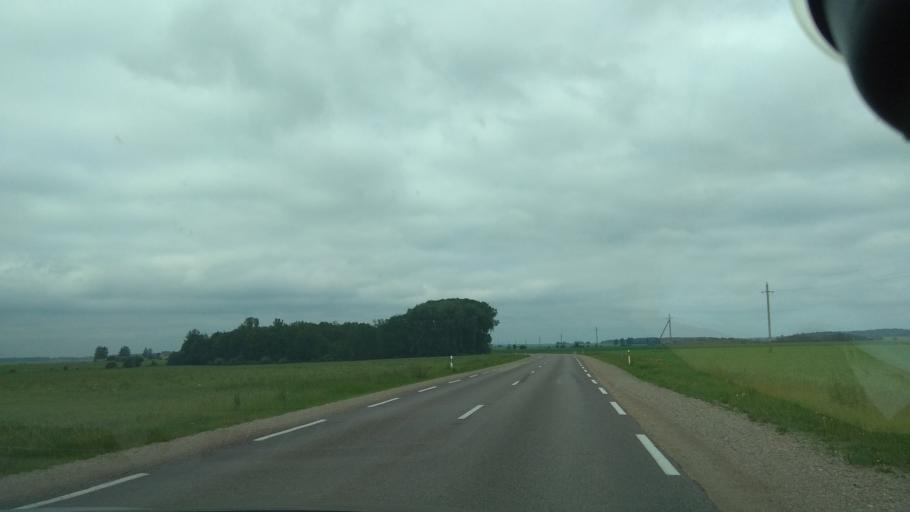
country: LT
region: Siauliu apskritis
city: Pakruojis
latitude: 55.8289
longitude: 23.9983
